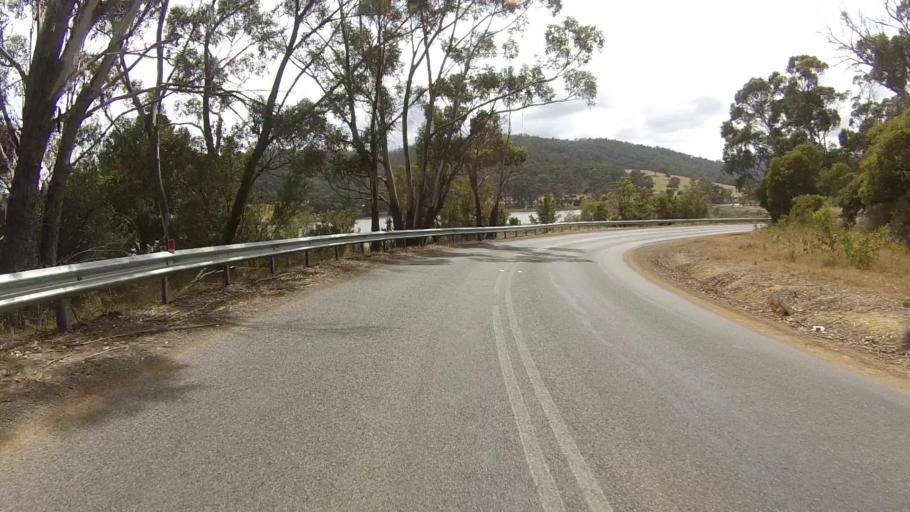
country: AU
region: Tasmania
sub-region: Huon Valley
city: Cygnet
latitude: -43.1882
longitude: 147.1004
